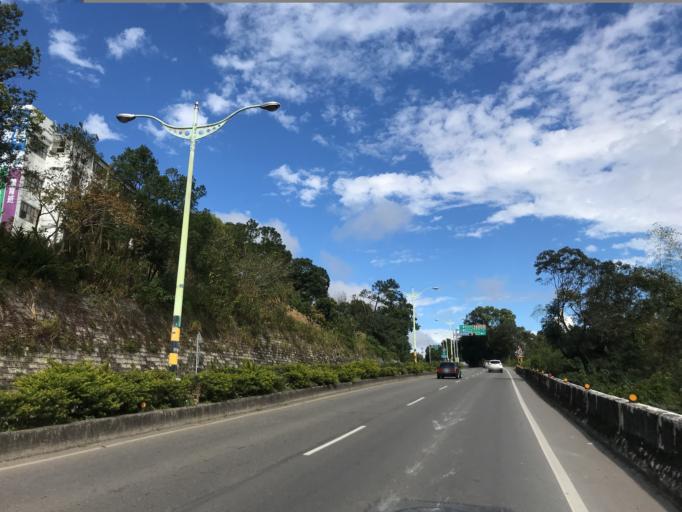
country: TW
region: Taiwan
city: Daxi
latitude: 24.8461
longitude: 121.2450
